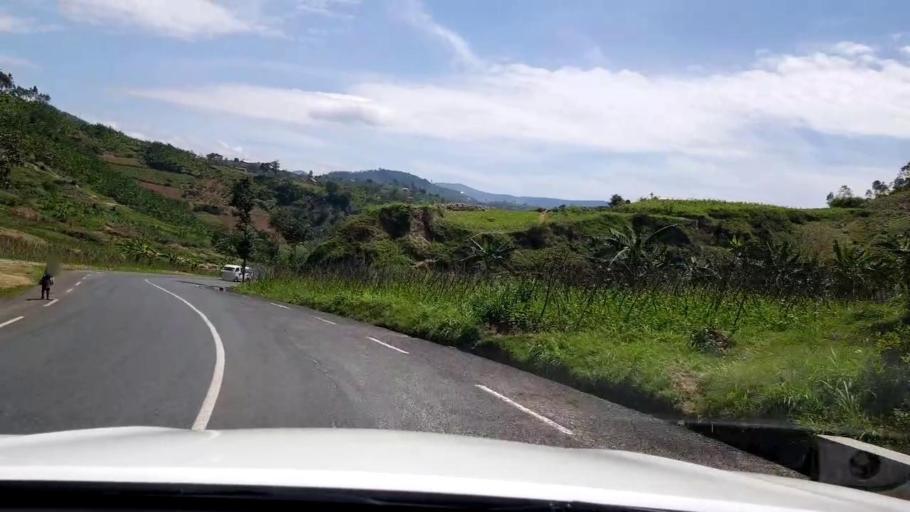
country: RW
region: Southern Province
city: Gitarama
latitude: -1.9186
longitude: 29.6347
